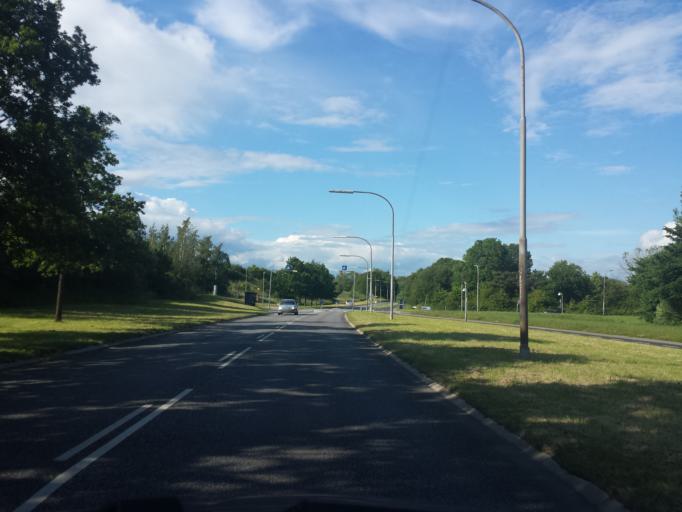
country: DK
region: Capital Region
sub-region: Ballerup Kommune
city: Malov
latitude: 55.7504
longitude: 12.3304
